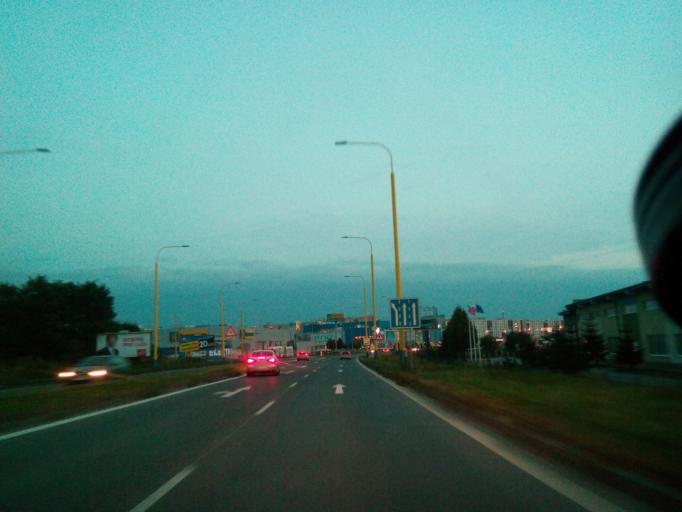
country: SK
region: Presovsky
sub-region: Okres Presov
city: Presov
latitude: 49.0015
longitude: 21.2684
